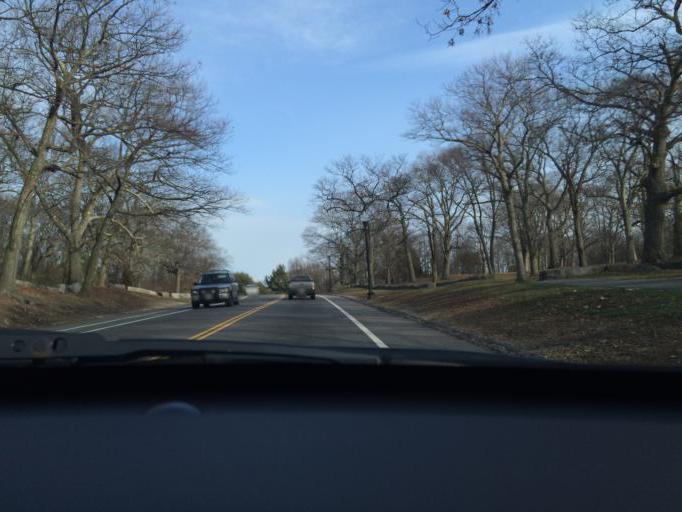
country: US
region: Massachusetts
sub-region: Suffolk County
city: Jamaica Plain
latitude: 42.3039
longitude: -71.0982
